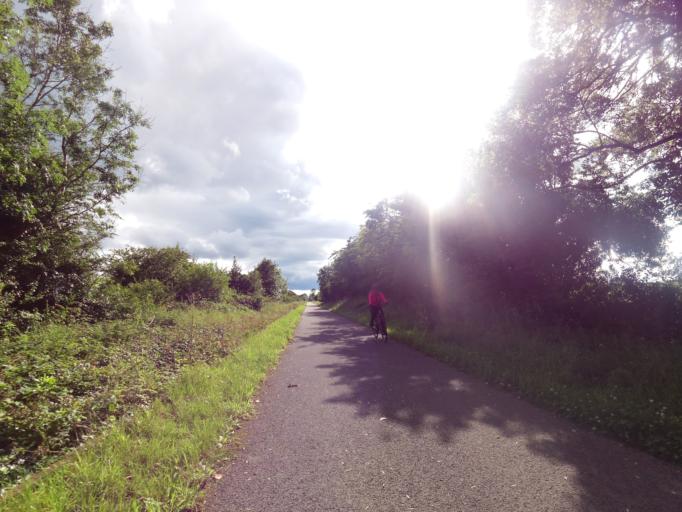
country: IE
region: Leinster
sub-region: An Iarmhi
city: Kilbeggan
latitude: 53.4832
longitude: -7.4684
